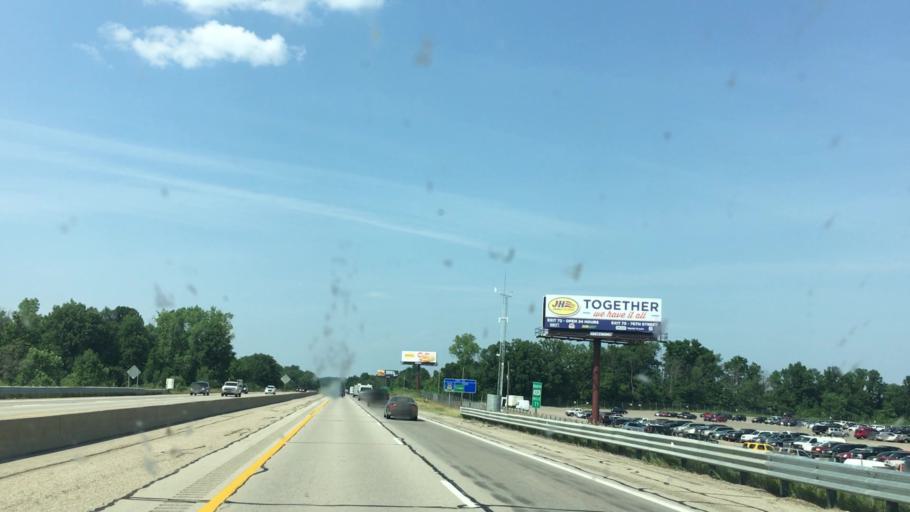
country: US
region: Michigan
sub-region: Kent County
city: Byron Center
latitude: 42.7657
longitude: -85.6725
